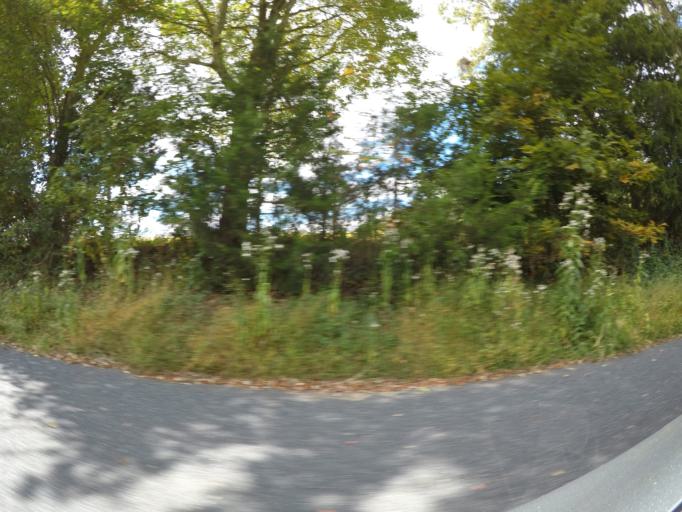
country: US
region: Maryland
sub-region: Harford County
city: Jarrettsville
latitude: 39.6899
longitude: -76.4988
